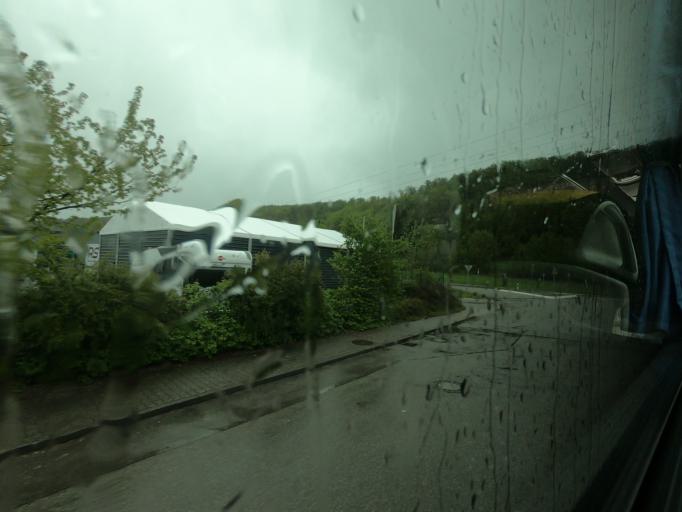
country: DE
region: Baden-Wuerttemberg
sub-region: Regierungsbezirk Stuttgart
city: Konigsbronn
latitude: 48.7358
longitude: 10.1327
